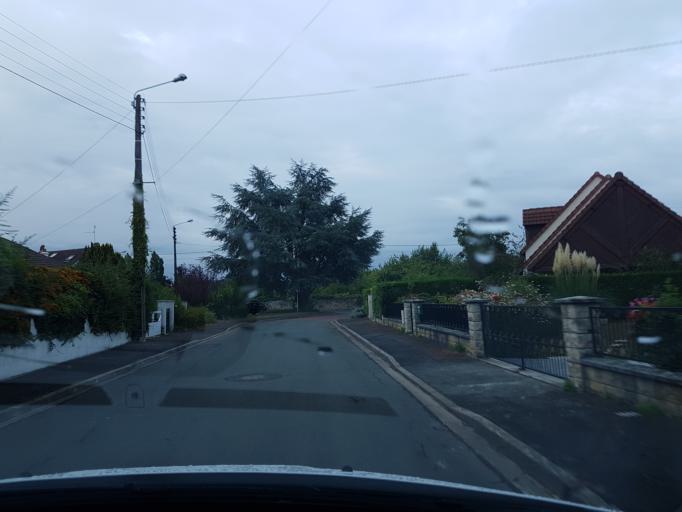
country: FR
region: Centre
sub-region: Departement d'Indre-et-Loire
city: Saint-Avertin
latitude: 47.3672
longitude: 0.7460
